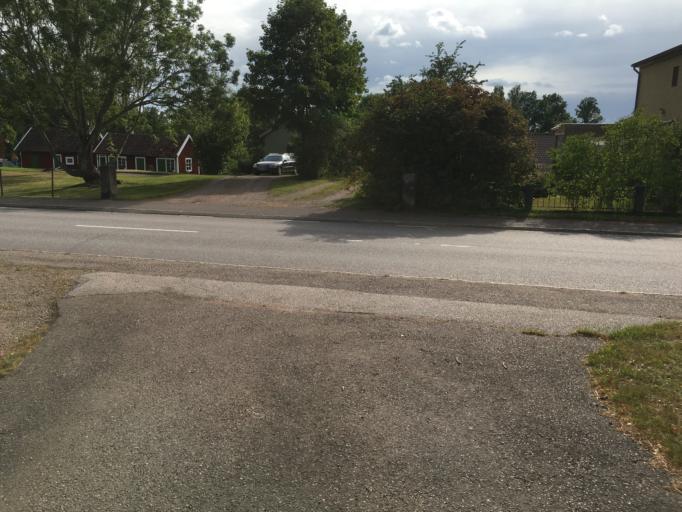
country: SE
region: Kalmar
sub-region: Nybro Kommun
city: Nybro
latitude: 56.9464
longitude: 15.9109
